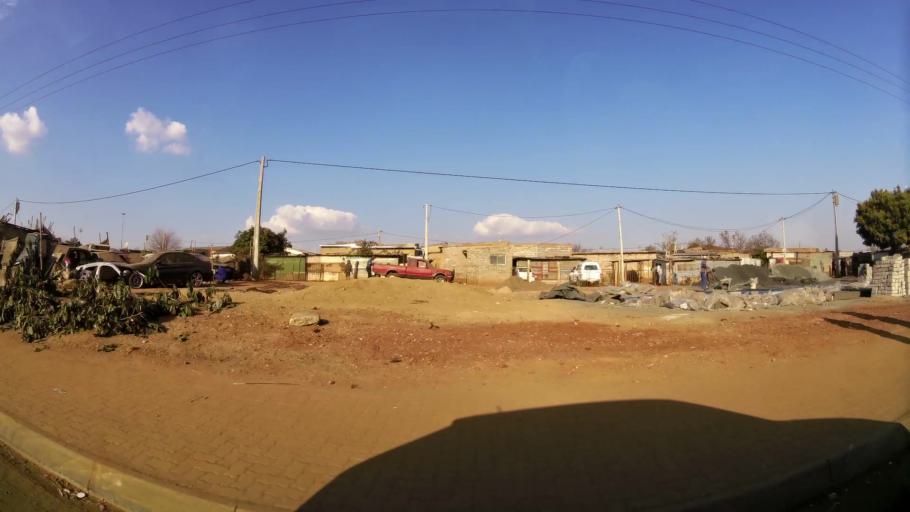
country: ZA
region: Gauteng
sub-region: Ekurhuleni Metropolitan Municipality
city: Tembisa
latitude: -25.9717
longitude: 28.2132
